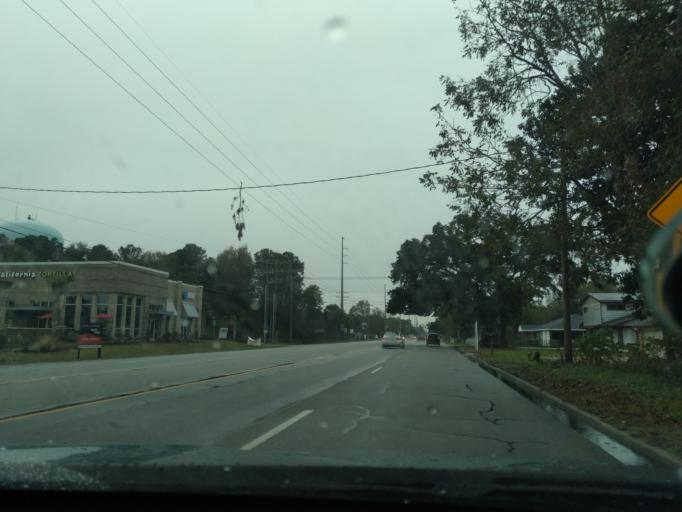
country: US
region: South Carolina
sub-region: Charleston County
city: Folly Beach
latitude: 32.7143
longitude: -79.9650
